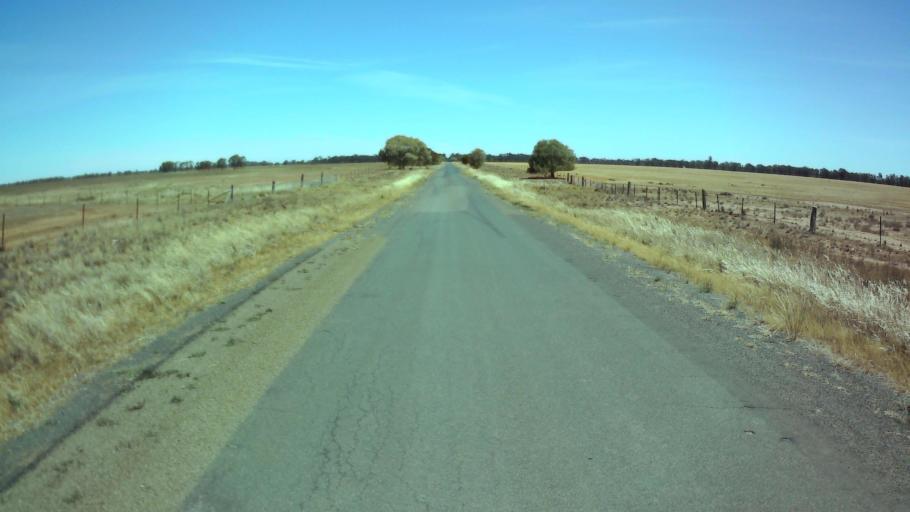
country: AU
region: New South Wales
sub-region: Weddin
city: Grenfell
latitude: -33.8521
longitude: 147.6954
